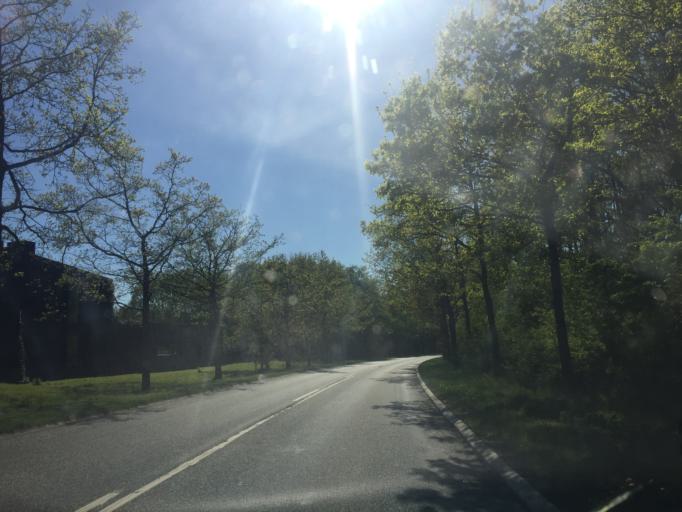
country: DK
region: Capital Region
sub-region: Herlev Kommune
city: Herlev
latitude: 55.7425
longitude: 12.4093
